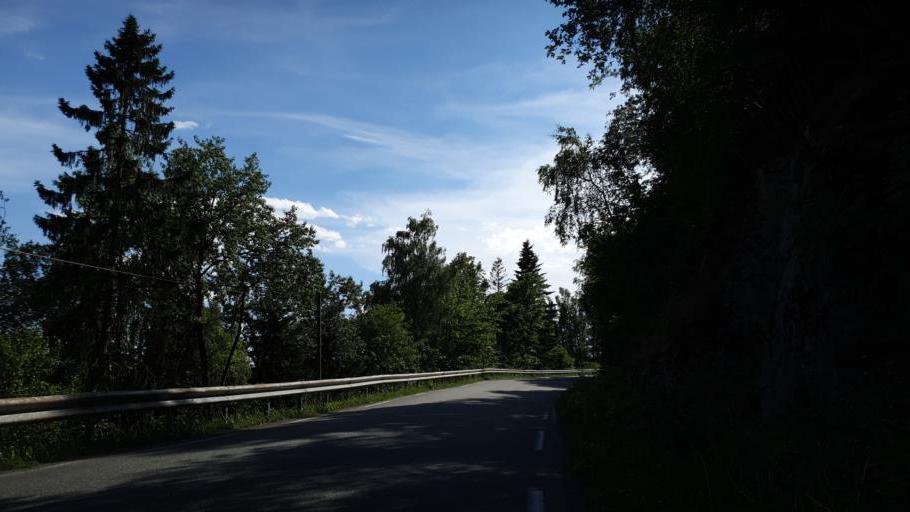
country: NO
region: Nord-Trondelag
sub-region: Leksvik
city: Leksvik
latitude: 63.6373
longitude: 10.5808
